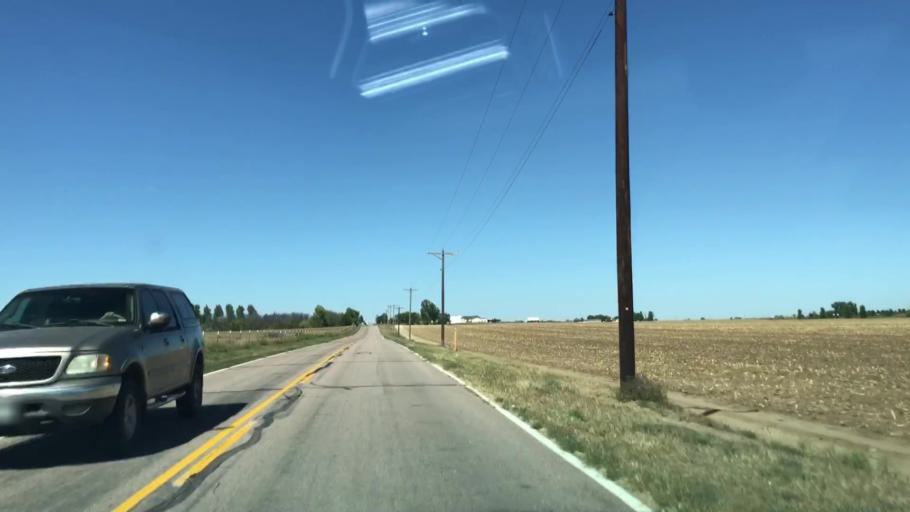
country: US
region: Colorado
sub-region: Weld County
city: Windsor
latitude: 40.5252
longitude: -104.9270
